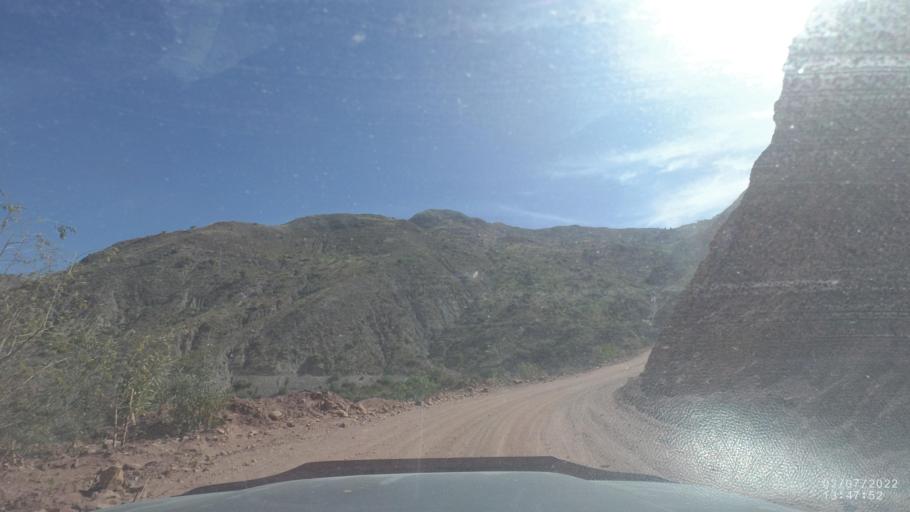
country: BO
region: Cochabamba
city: Irpa Irpa
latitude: -17.8182
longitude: -66.3714
